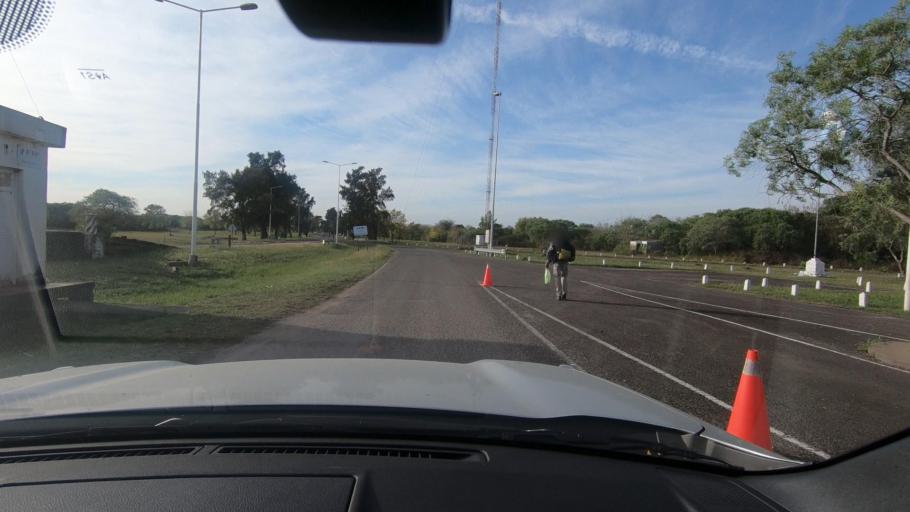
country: AR
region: Entre Rios
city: Colon
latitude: -32.2452
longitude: -58.1902
